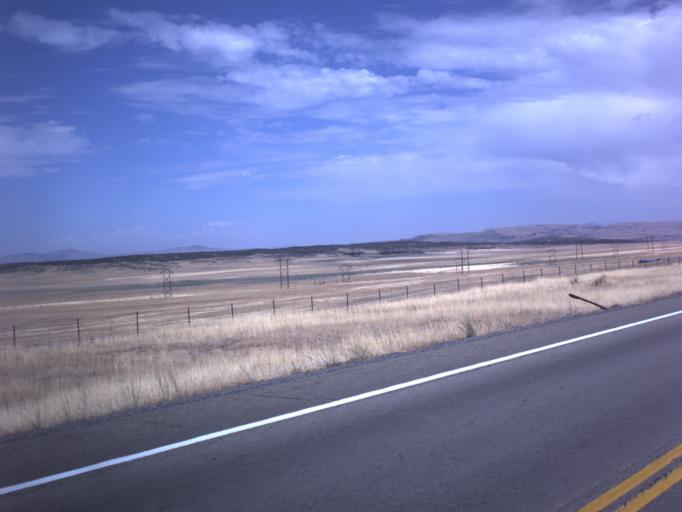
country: US
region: Utah
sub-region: Sanpete County
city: Gunnison
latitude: 39.4037
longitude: -111.9277
